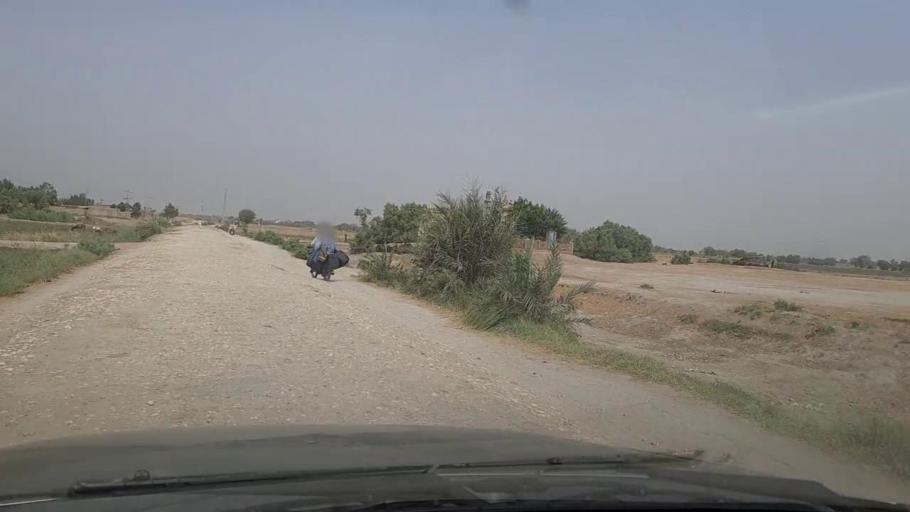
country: PK
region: Balochistan
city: Sohbatpur
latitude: 28.4168
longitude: 68.6860
